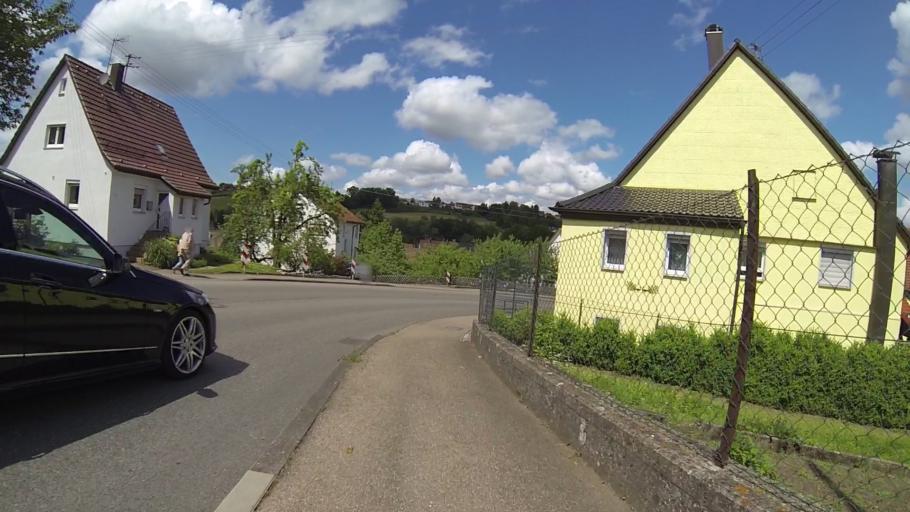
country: DE
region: Baden-Wuerttemberg
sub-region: Regierungsbezirk Stuttgart
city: Waldstetten
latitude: 48.7830
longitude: 9.8392
